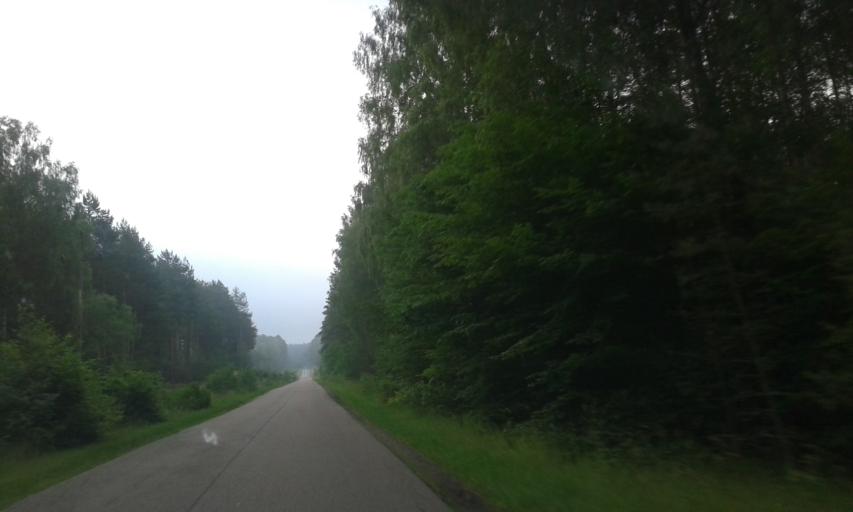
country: PL
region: Kujawsko-Pomorskie
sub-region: Powiat sepolenski
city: Sypniewo
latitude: 53.4556
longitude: 17.3442
